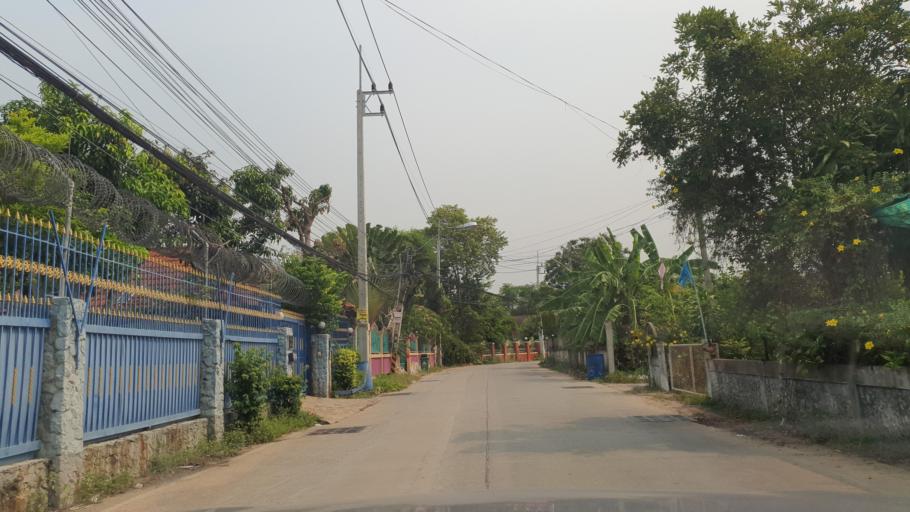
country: TH
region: Chon Buri
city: Phatthaya
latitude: 12.8925
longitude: 100.8852
